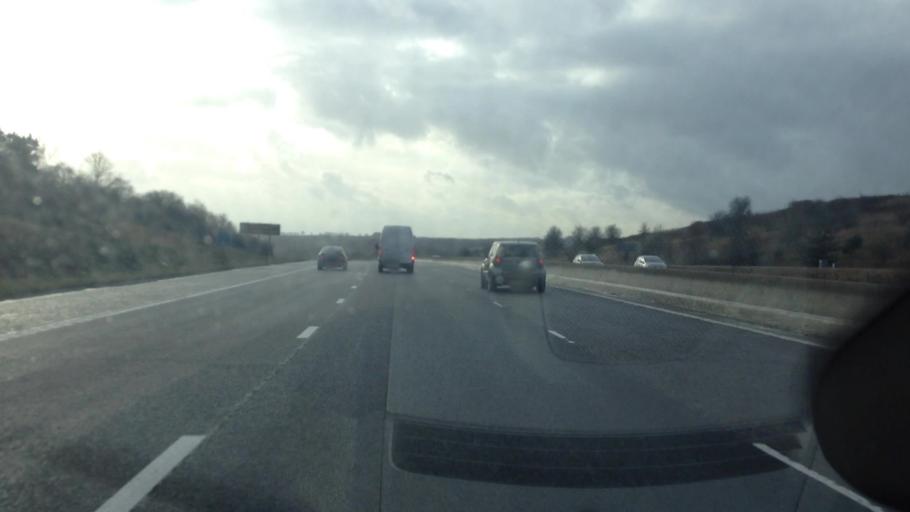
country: GB
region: England
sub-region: City and Borough of Wakefield
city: Crigglestone
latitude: 53.6194
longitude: -1.5499
